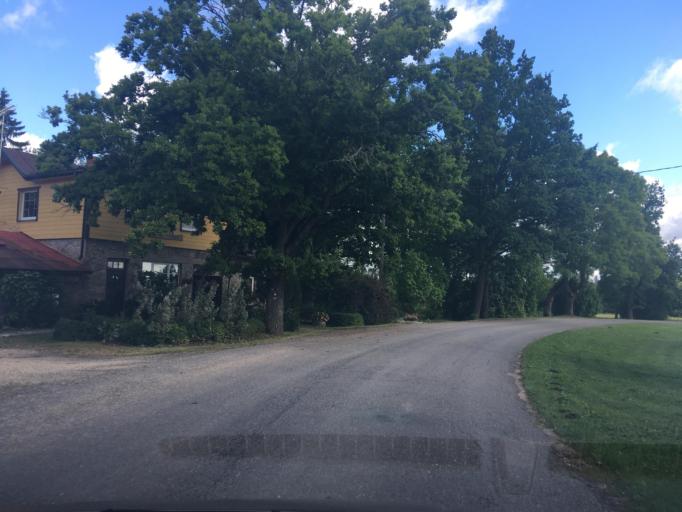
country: EE
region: Jogevamaa
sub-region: Poltsamaa linn
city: Poltsamaa
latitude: 58.4707
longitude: 25.9561
